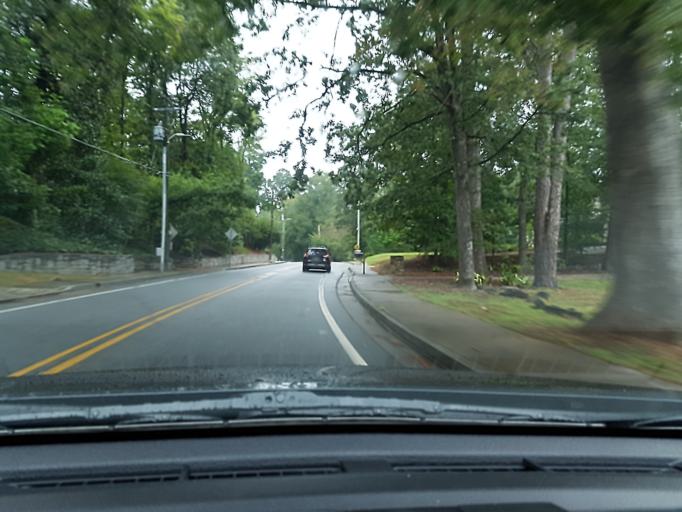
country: US
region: Georgia
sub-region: DeKalb County
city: North Atlanta
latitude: 33.8637
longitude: -84.3681
